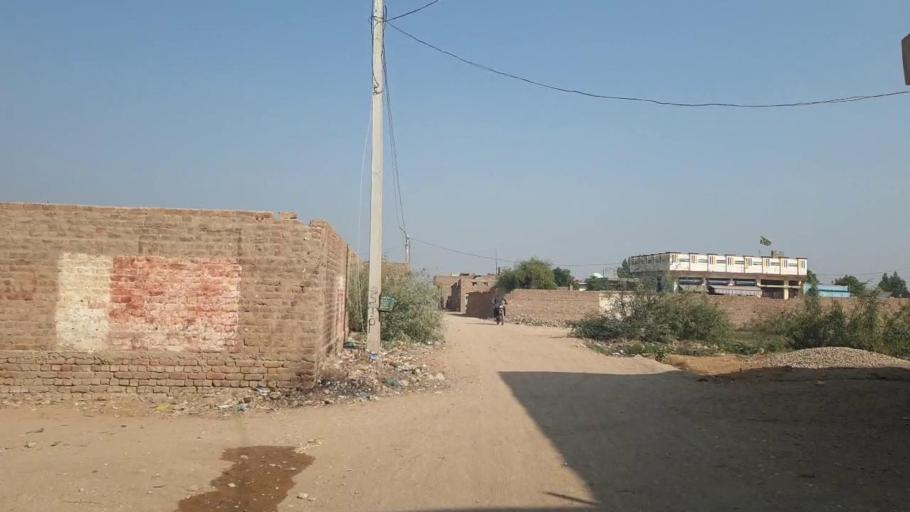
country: PK
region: Sindh
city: Jamshoro
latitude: 25.4124
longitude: 68.2838
